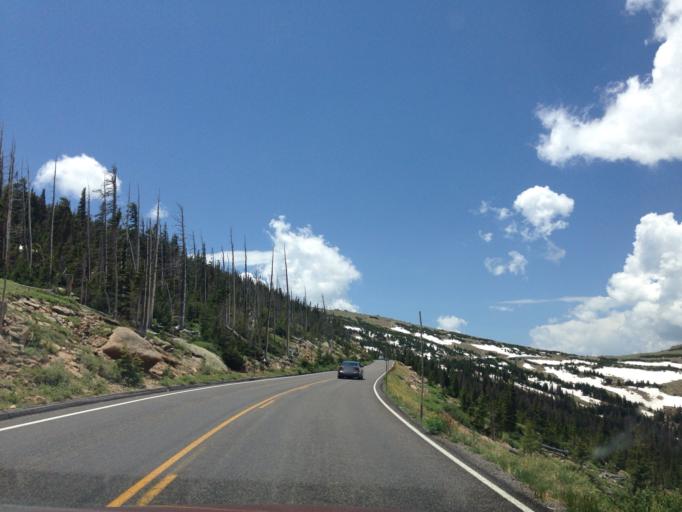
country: US
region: Colorado
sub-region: Larimer County
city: Estes Park
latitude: 40.3951
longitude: -105.6809
